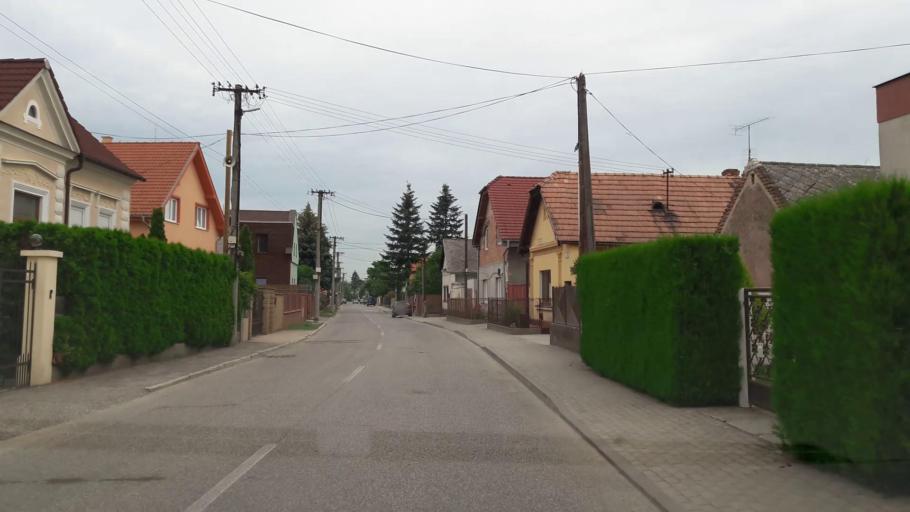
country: SK
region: Bratislavsky
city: Senec
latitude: 48.2097
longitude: 17.3610
